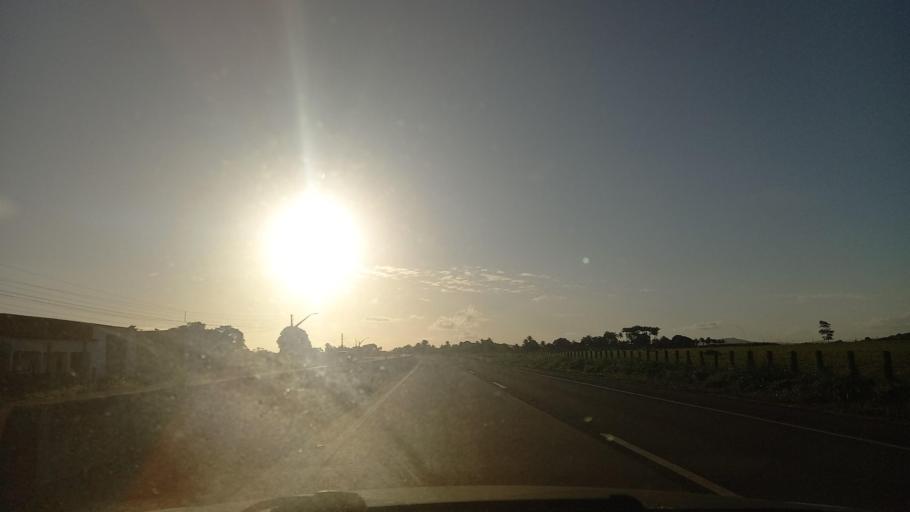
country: BR
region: Alagoas
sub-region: Limoeiro De Anadia
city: Cajueiro
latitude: -9.7445
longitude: -36.4644
